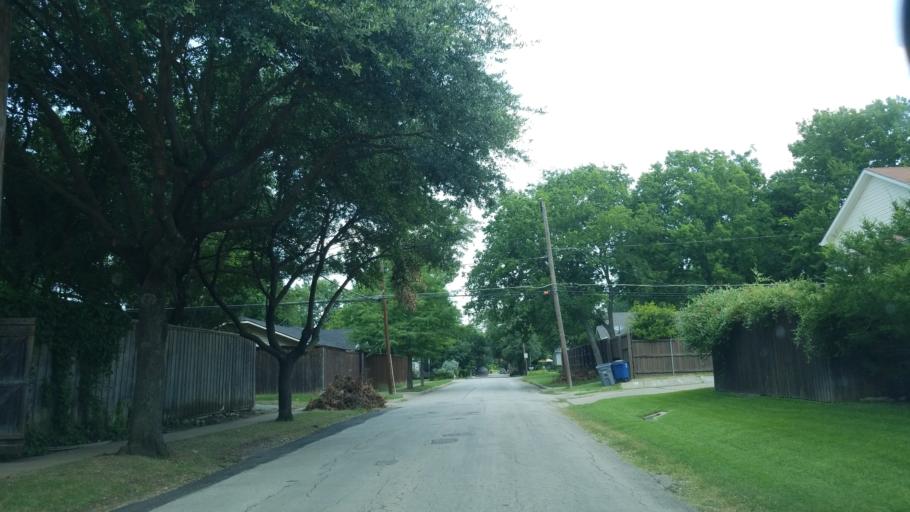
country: US
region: Texas
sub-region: Dallas County
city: Highland Park
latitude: 32.8226
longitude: -96.7774
